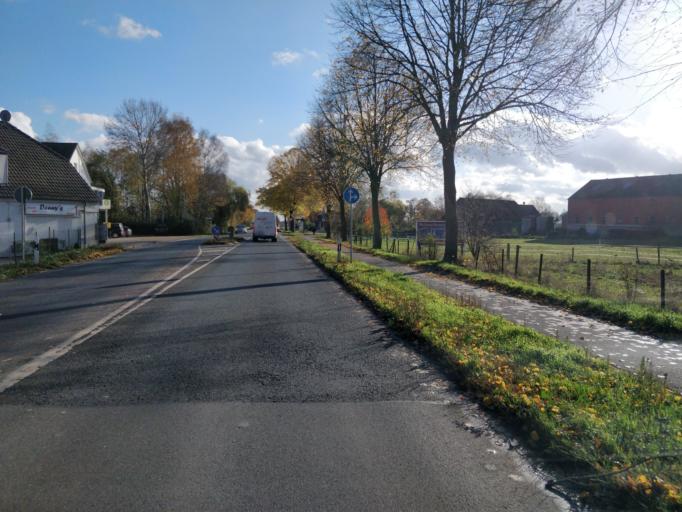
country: DE
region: North Rhine-Westphalia
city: Rees
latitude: 51.8006
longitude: 6.3692
